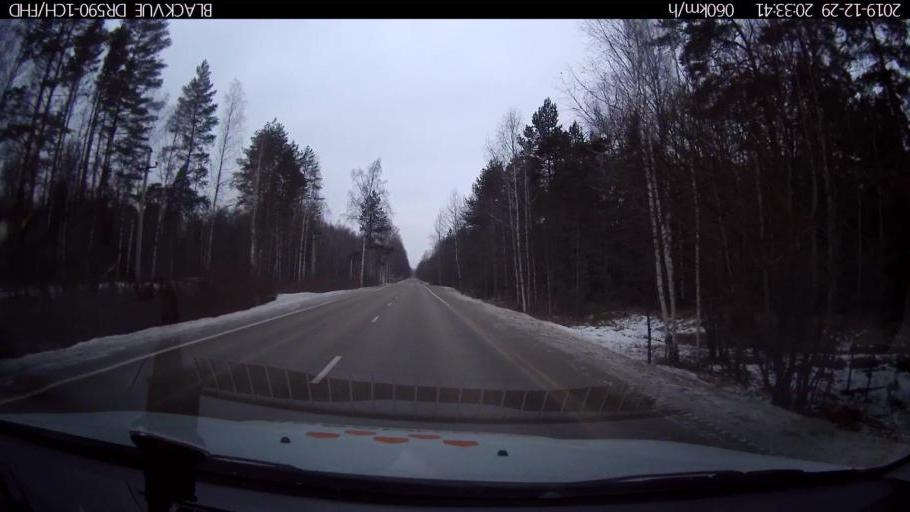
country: RU
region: Nizjnij Novgorod
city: Afonino
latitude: 56.1819
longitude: 44.0488
